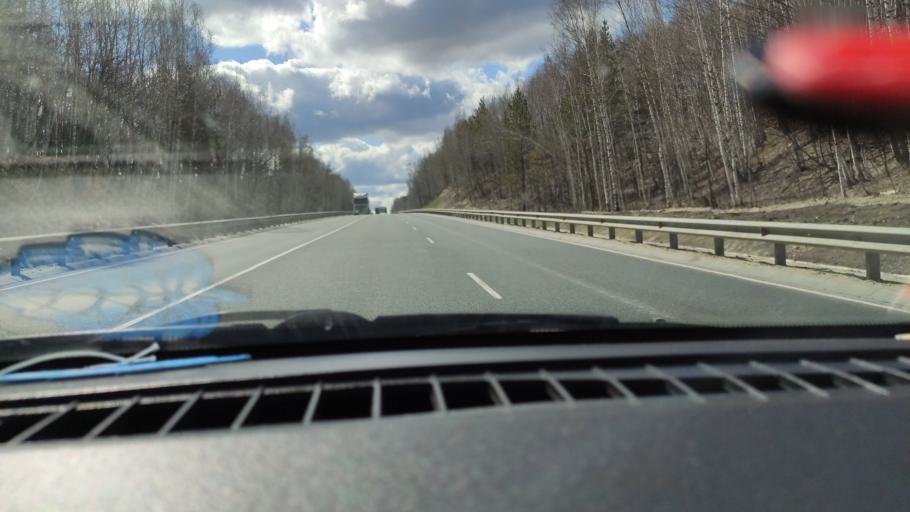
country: RU
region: Saratov
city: Khvalynsk
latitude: 52.5000
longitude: 48.0148
